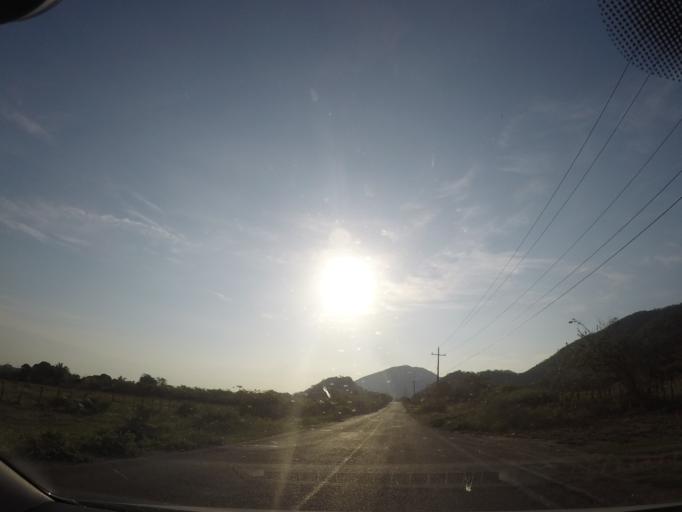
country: MX
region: Oaxaca
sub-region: Santo Domingo Tehuantepec
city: La Noria
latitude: 16.2350
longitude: -95.1708
